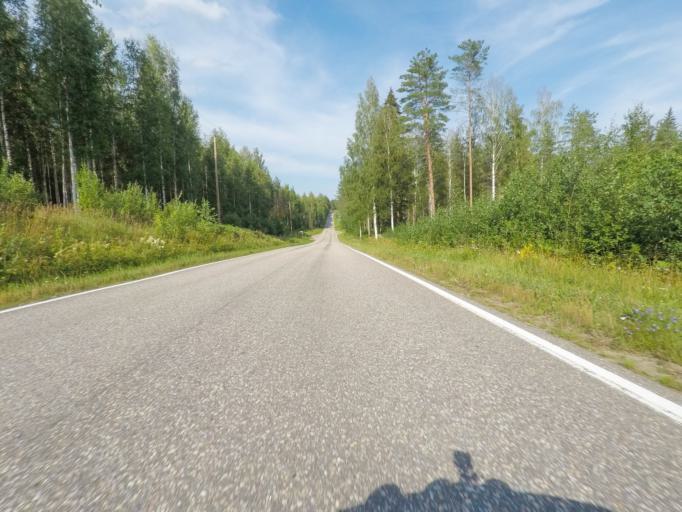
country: FI
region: Southern Savonia
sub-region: Savonlinna
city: Sulkava
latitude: 61.7583
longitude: 28.2278
